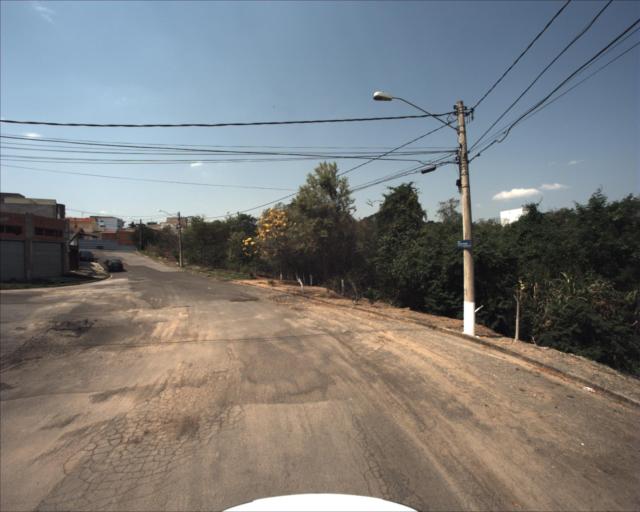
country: BR
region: Sao Paulo
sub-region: Sorocaba
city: Sorocaba
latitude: -23.4433
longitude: -47.4815
